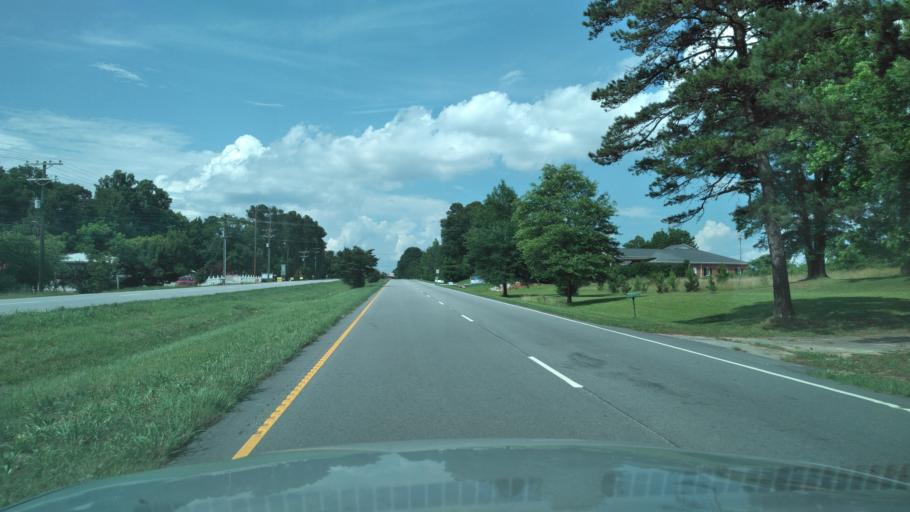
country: US
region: South Carolina
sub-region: Spartanburg County
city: Roebuck
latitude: 34.8576
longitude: -81.9642
